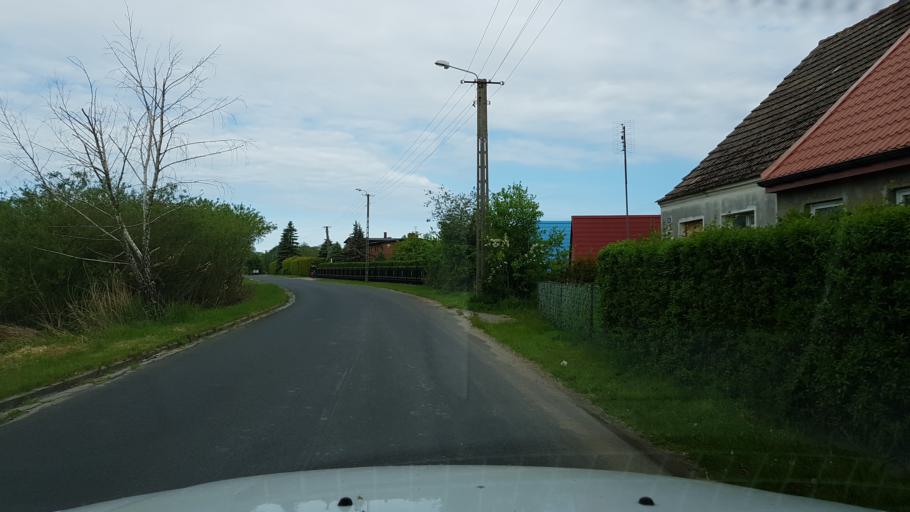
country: PL
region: West Pomeranian Voivodeship
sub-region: Powiat kolobrzeski
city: Ustronie Morskie
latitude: 54.2188
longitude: 15.8130
